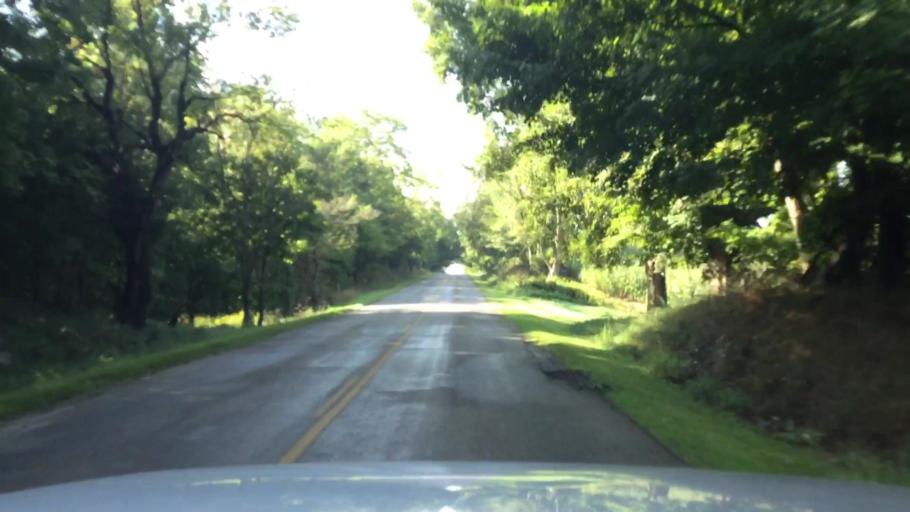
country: US
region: Michigan
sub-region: Lenawee County
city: Hudson
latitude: 41.9232
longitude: -84.4205
